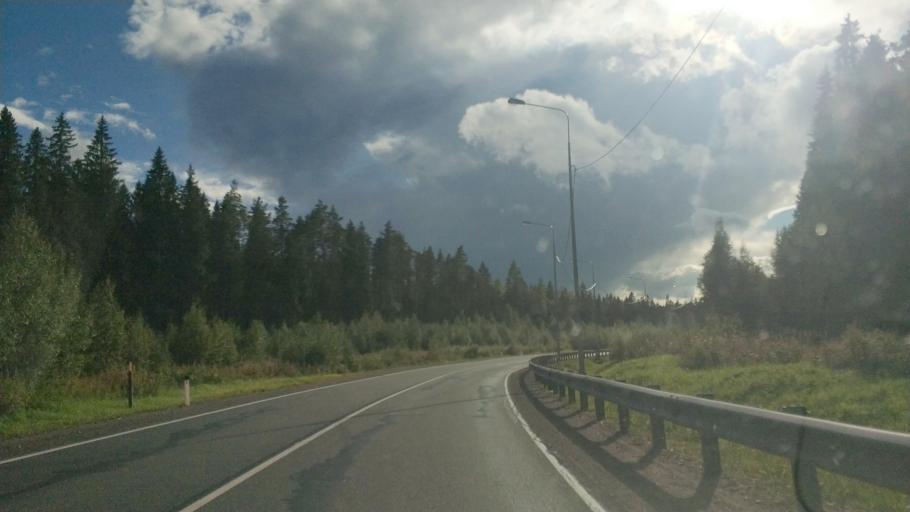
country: RU
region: Republic of Karelia
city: Lakhdenpokh'ya
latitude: 61.5108
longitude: 30.0963
